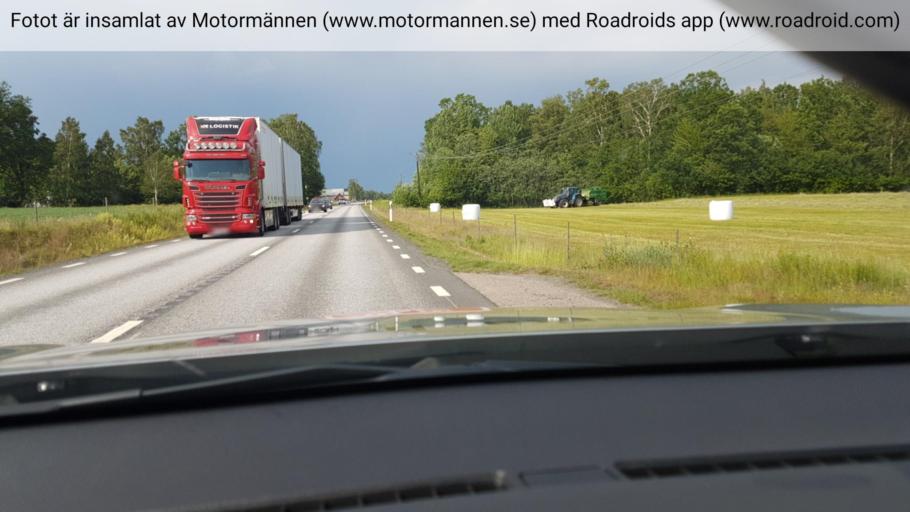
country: SE
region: Joenkoeping
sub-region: Habo Kommun
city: Habo
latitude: 58.0543
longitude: 14.1880
